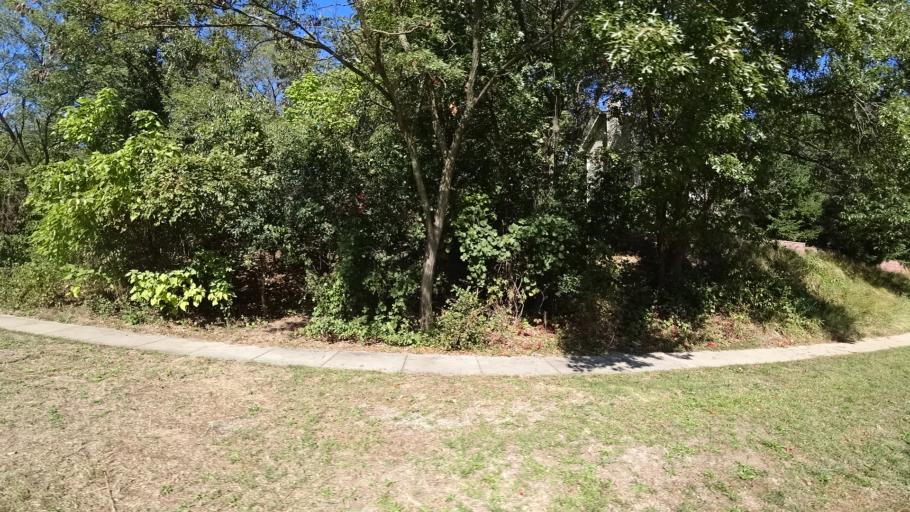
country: US
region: Indiana
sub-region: LaPorte County
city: Michigan City
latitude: 41.7272
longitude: -86.8903
